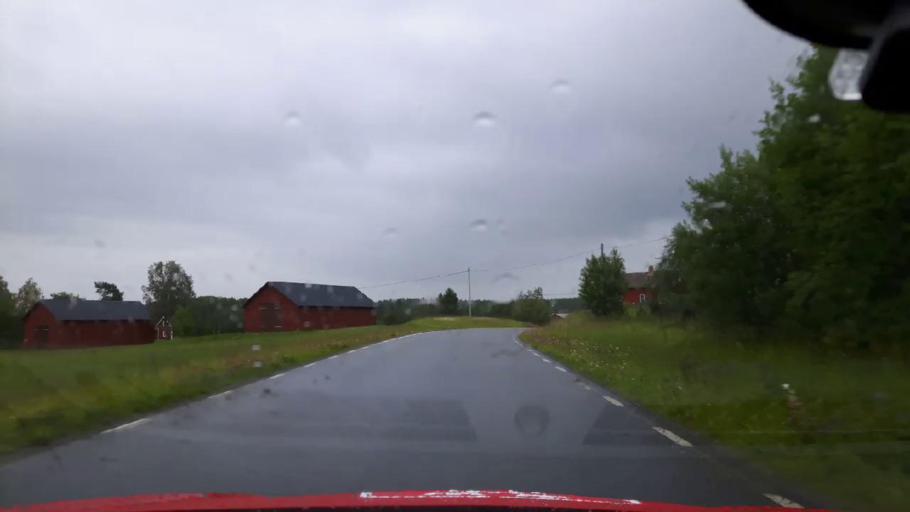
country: SE
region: Jaemtland
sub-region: OEstersunds Kommun
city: Brunflo
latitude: 63.0123
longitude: 14.7329
